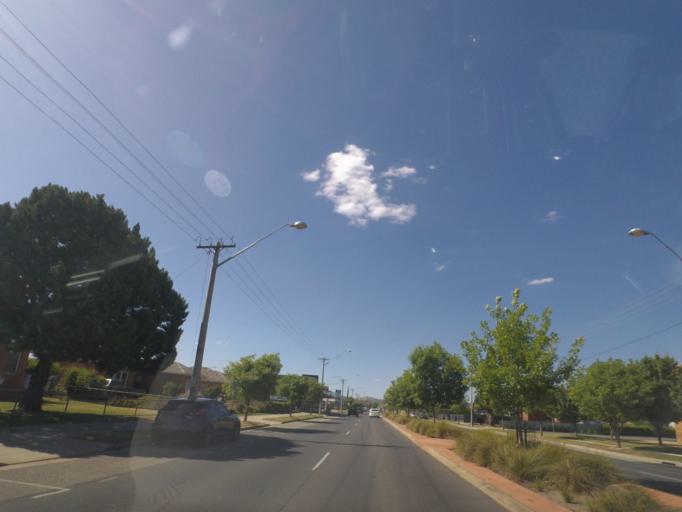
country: AU
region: New South Wales
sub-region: Albury Municipality
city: North Albury
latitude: -36.0586
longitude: 146.9324
